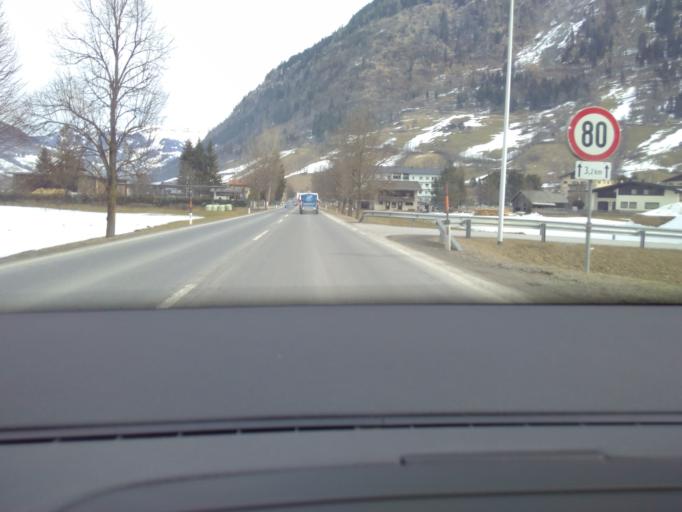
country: AT
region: Salzburg
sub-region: Politischer Bezirk Sankt Johann im Pongau
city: Bad Hofgastein
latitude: 47.1738
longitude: 13.0990
